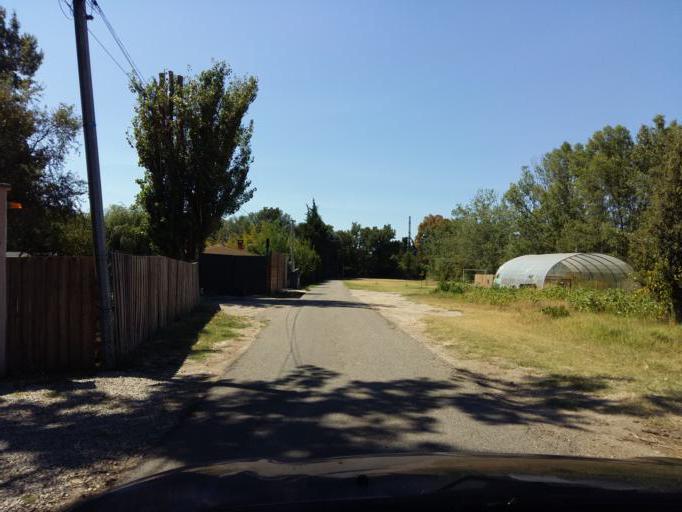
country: FR
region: Provence-Alpes-Cote d'Azur
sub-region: Departement du Vaucluse
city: Loriol-du-Comtat
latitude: 44.0884
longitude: 5.0089
